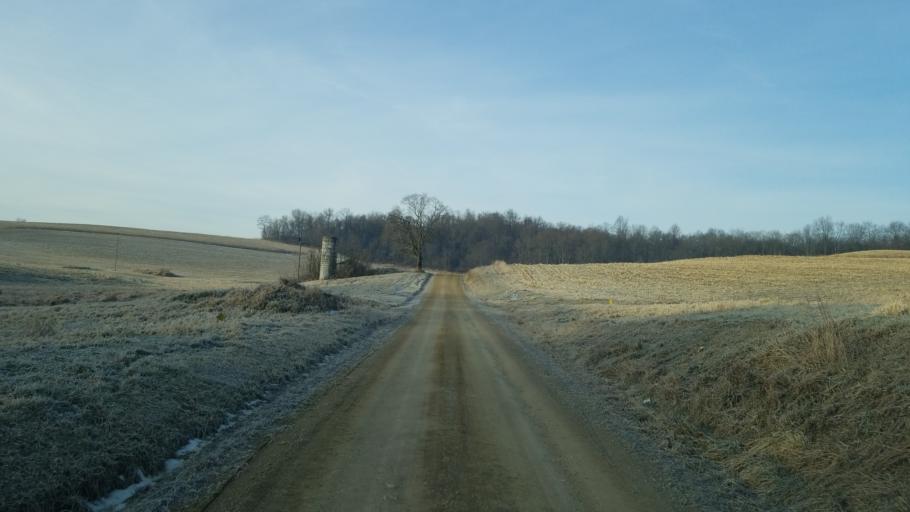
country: US
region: Pennsylvania
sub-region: Indiana County
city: Chevy Chase Heights
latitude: 40.8597
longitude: -79.2453
